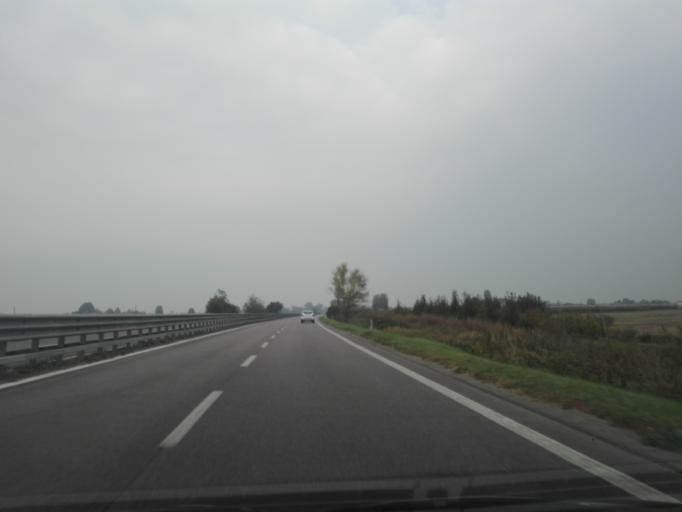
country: IT
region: Veneto
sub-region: Provincia di Verona
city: Villa Bartolomea
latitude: 45.1548
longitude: 11.3255
